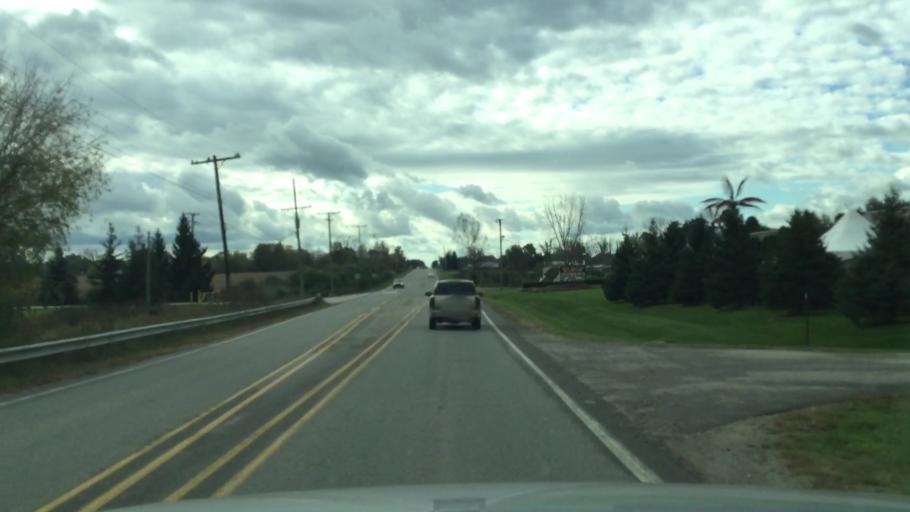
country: US
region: Michigan
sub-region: Lapeer County
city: Lapeer
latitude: 43.0407
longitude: -83.3619
